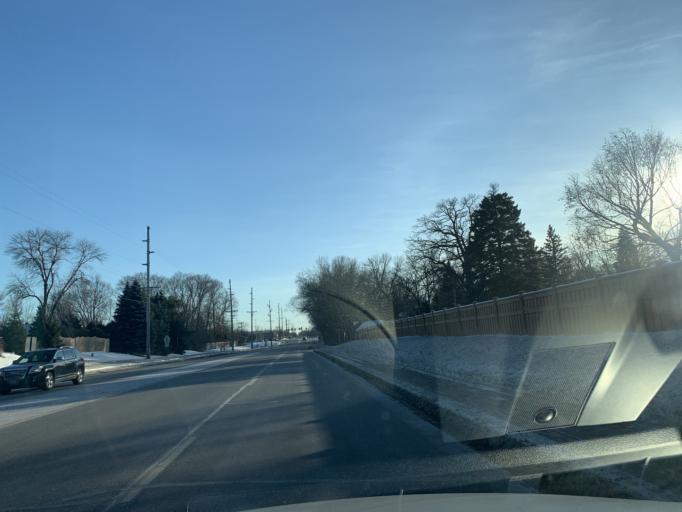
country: US
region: Minnesota
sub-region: Hennepin County
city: Wayzata
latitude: 44.9798
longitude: -93.5022
